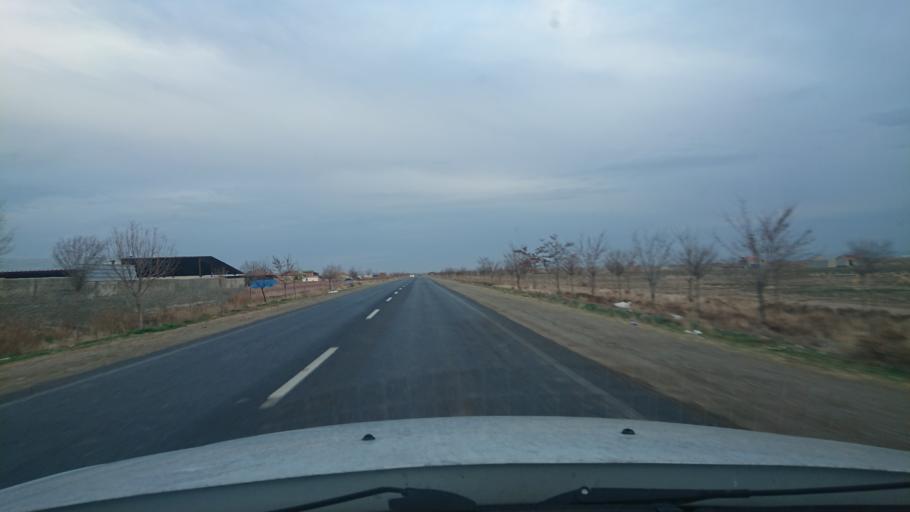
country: TR
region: Aksaray
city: Yesilova
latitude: 38.3013
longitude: 33.7569
